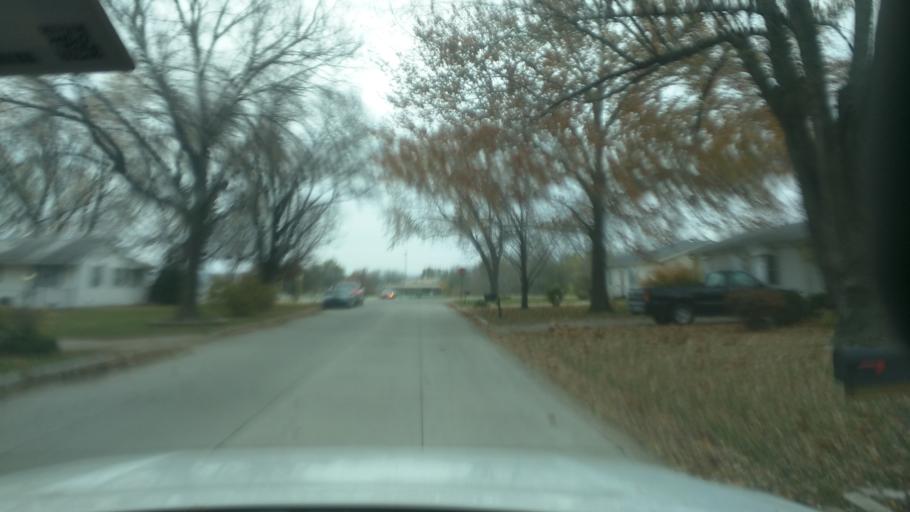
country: US
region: Kansas
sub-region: Riley County
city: Manhattan
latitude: 39.1996
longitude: -96.5595
